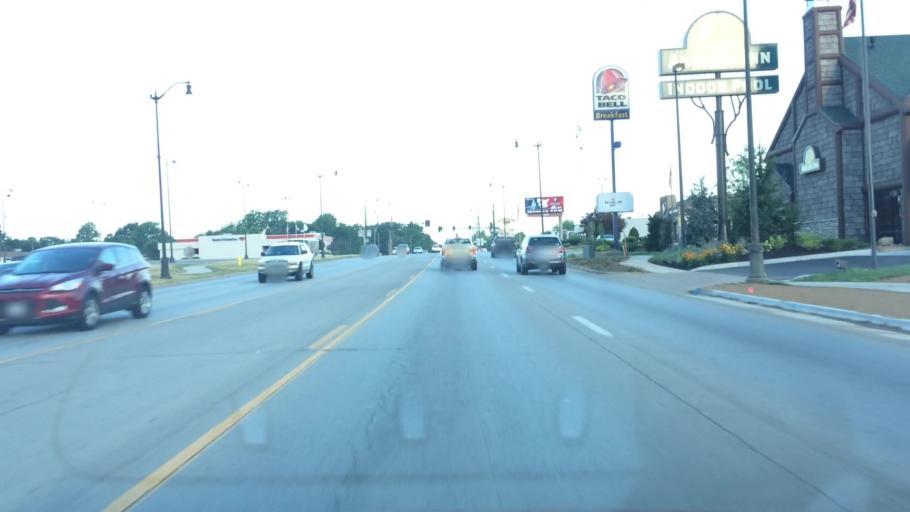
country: US
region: Missouri
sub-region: Greene County
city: Springfield
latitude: 37.1823
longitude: -93.2980
